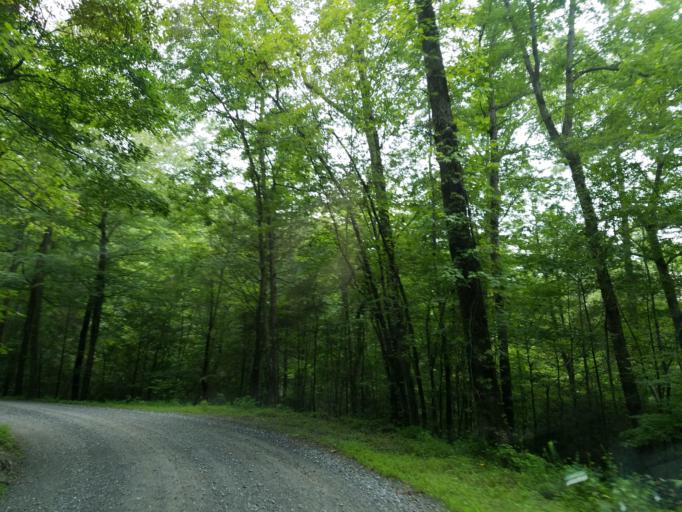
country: US
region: Georgia
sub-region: Fannin County
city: Blue Ridge
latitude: 34.8158
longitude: -84.2395
